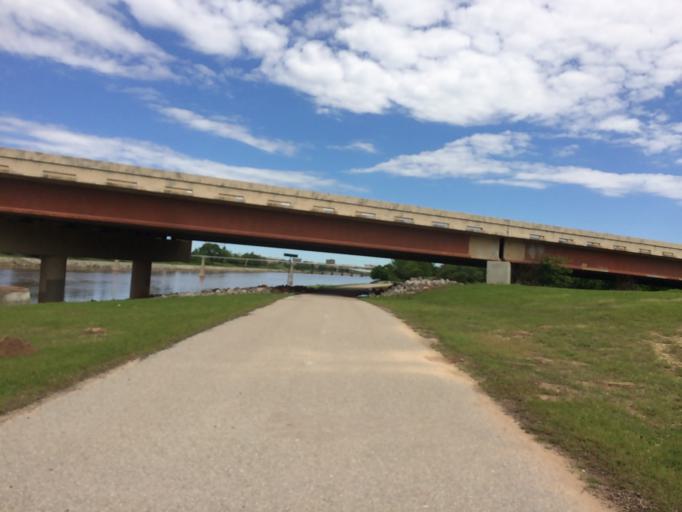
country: US
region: Oklahoma
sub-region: Oklahoma County
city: Oklahoma City
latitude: 35.4494
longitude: -97.5100
